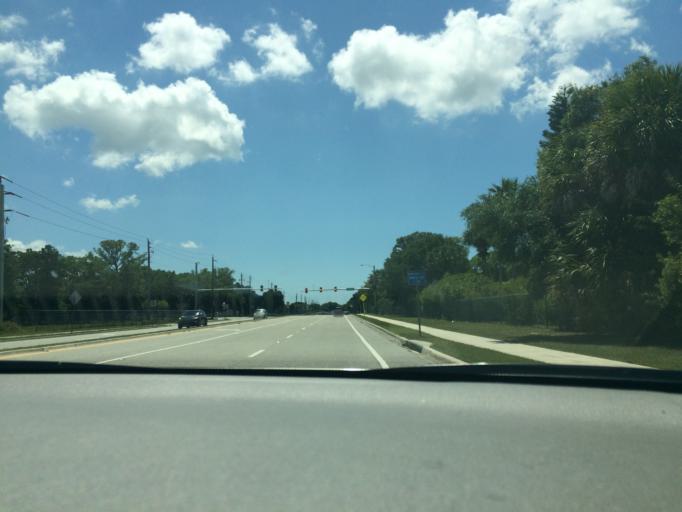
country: US
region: Florida
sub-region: Manatee County
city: Samoset
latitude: 27.4530
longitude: -82.4852
